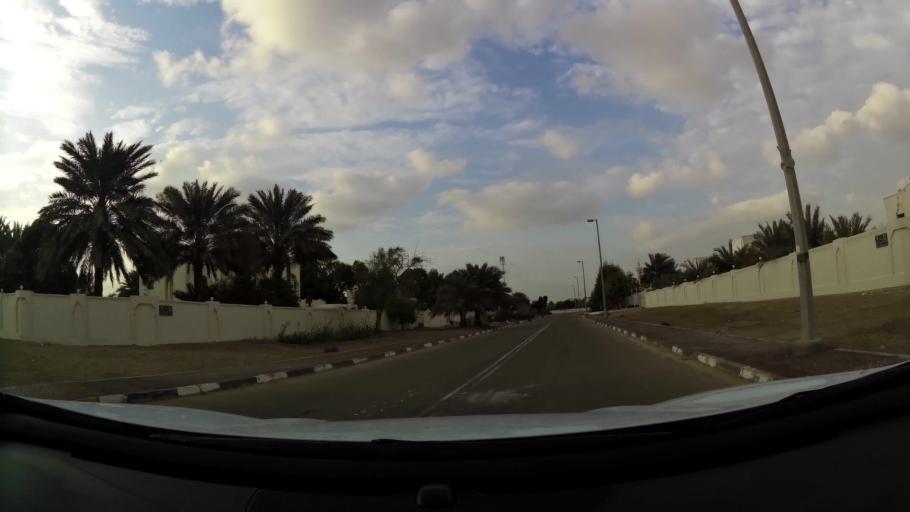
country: AE
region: Abu Dhabi
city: Abu Dhabi
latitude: 24.3788
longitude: 54.5308
